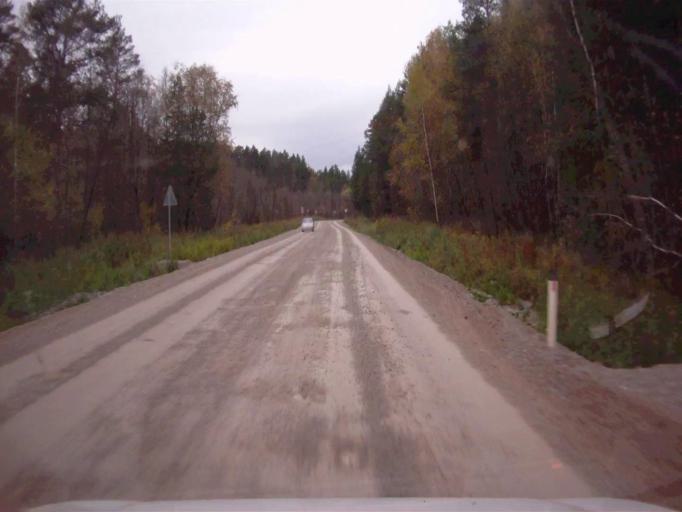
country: RU
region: Chelyabinsk
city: Nyazepetrovsk
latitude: 56.0447
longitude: 59.5048
